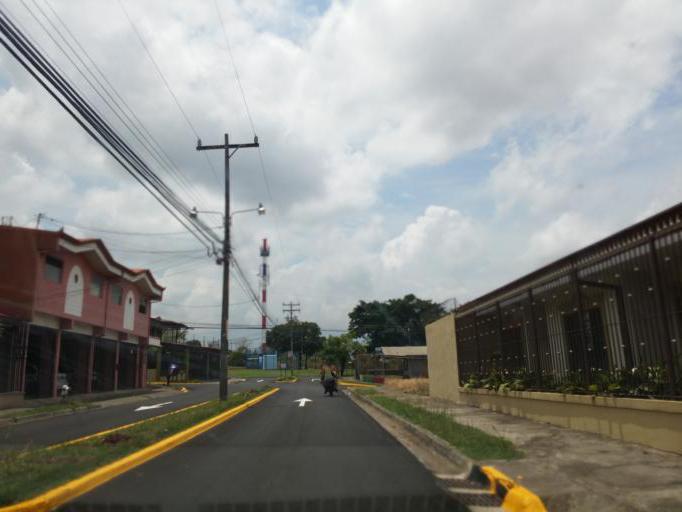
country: CR
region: Alajuela
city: Alajuela
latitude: 10.0267
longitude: -84.2038
